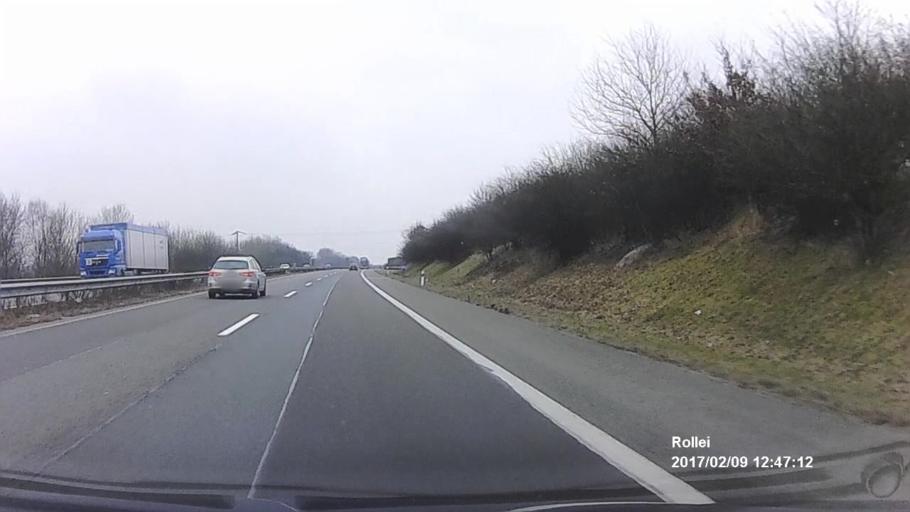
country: DE
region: Lower Saxony
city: Leer
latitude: 53.2639
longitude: 7.4604
